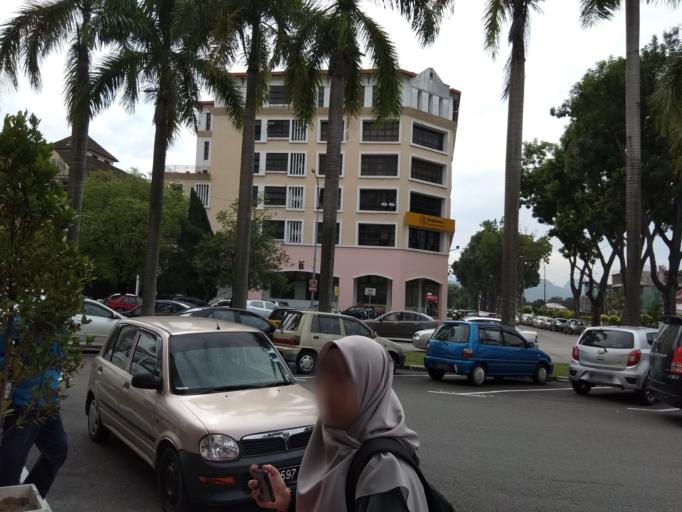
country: MY
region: Perak
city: Ipoh
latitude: 4.5985
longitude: 101.0940
